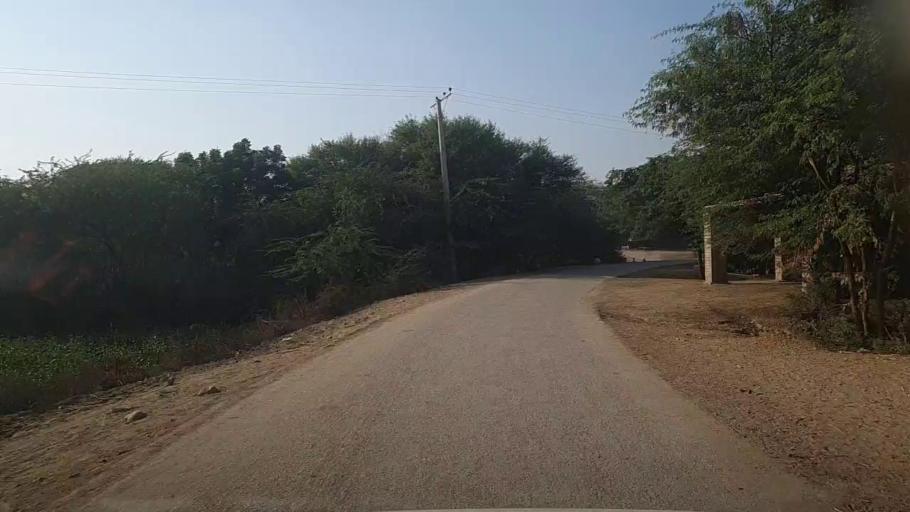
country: PK
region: Sindh
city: Karaundi
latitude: 26.7877
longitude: 68.4678
